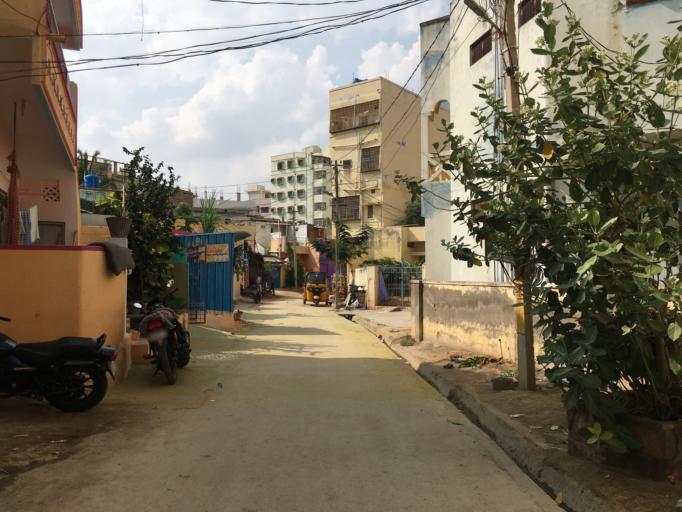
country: IN
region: Andhra Pradesh
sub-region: Anantapur
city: Puttaparthi
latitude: 14.1682
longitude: 77.8127
